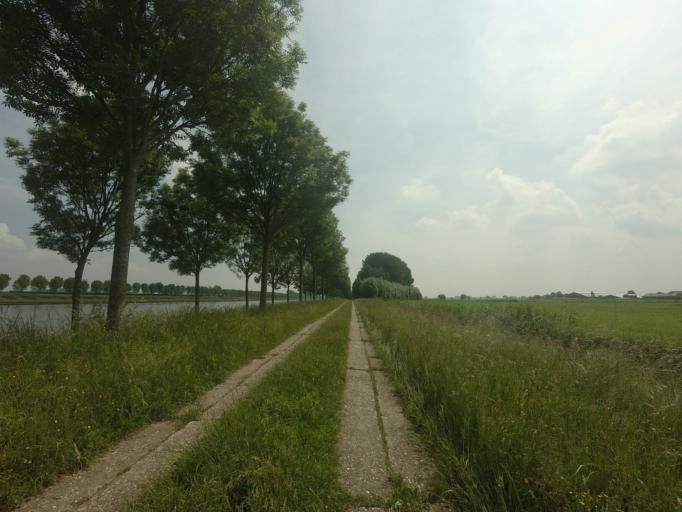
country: NL
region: Gelderland
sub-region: Gemeente Culemborg
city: Culemborg
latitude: 51.9852
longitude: 5.2541
